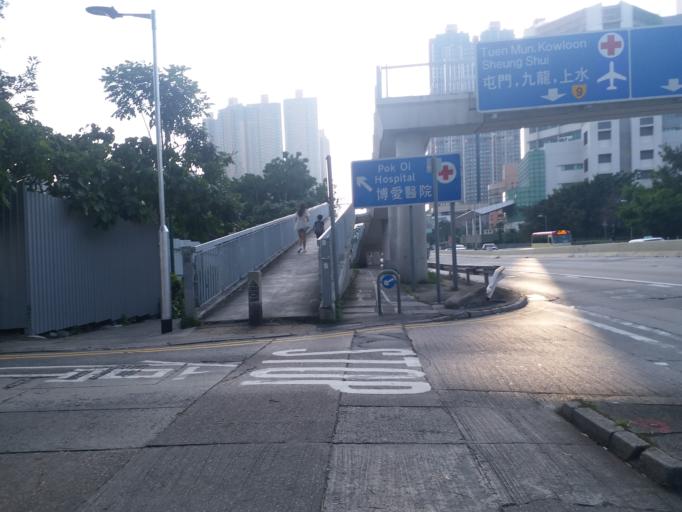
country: HK
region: Yuen Long
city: Yuen Long Kau Hui
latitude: 22.4442
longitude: 114.0433
